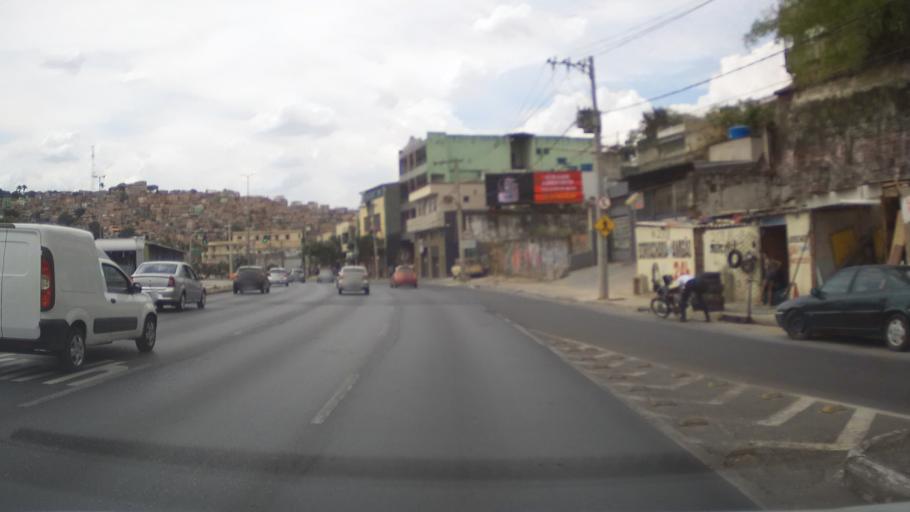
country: BR
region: Minas Gerais
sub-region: Belo Horizonte
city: Belo Horizonte
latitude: -19.8899
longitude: -43.9496
